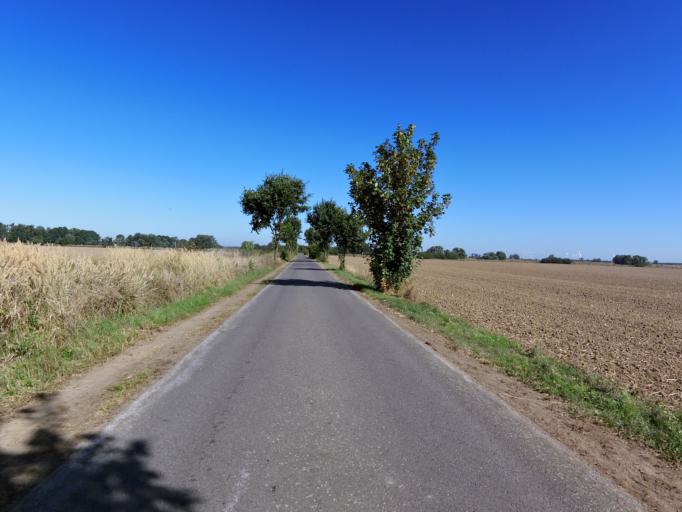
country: DE
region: Saxony
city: Elsnig
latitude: 51.6250
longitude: 12.9278
